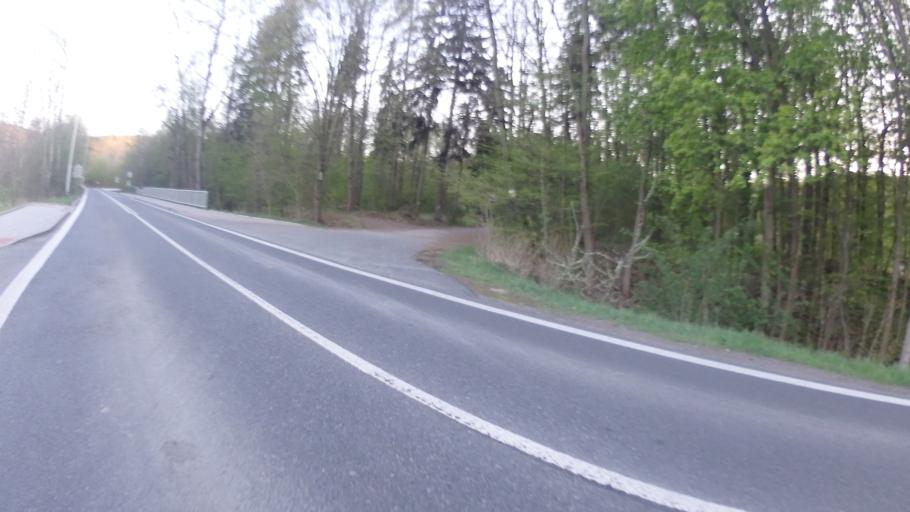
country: CZ
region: South Moravian
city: Troubsko
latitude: 49.1995
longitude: 16.5171
